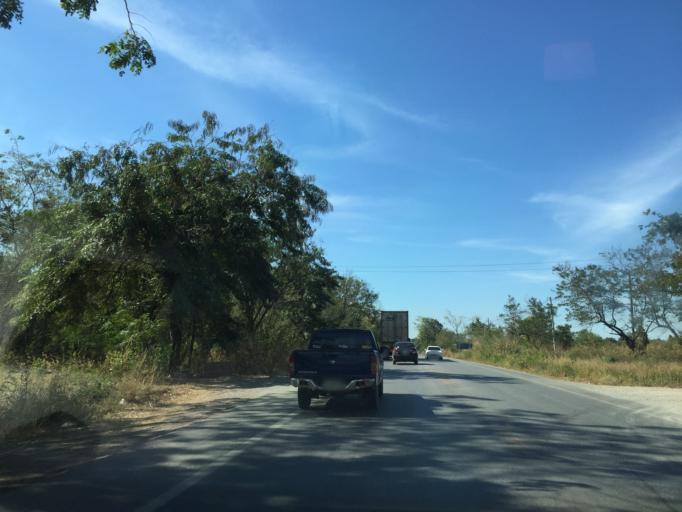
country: TH
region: Changwat Nong Bua Lamphu
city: Na Klang
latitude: 17.3133
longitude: 102.1682
